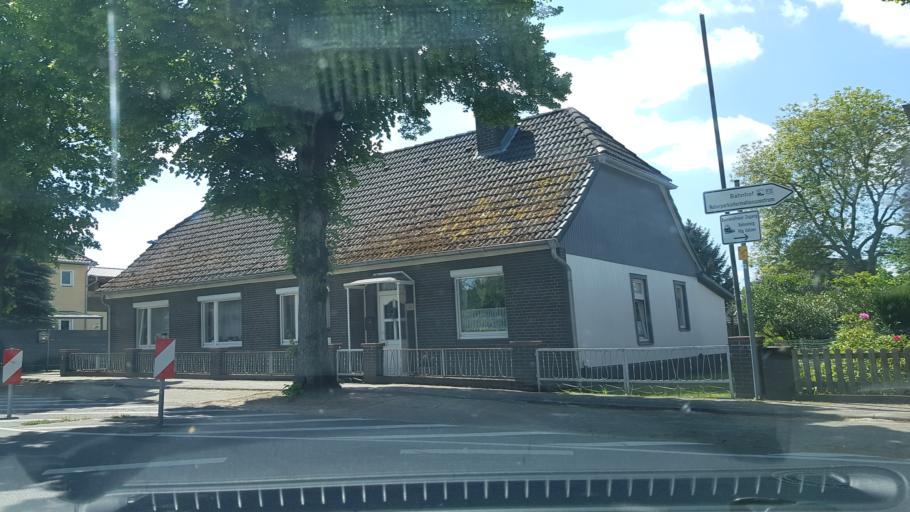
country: DE
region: Lower Saxony
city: Eschede
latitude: 52.7387
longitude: 10.2317
